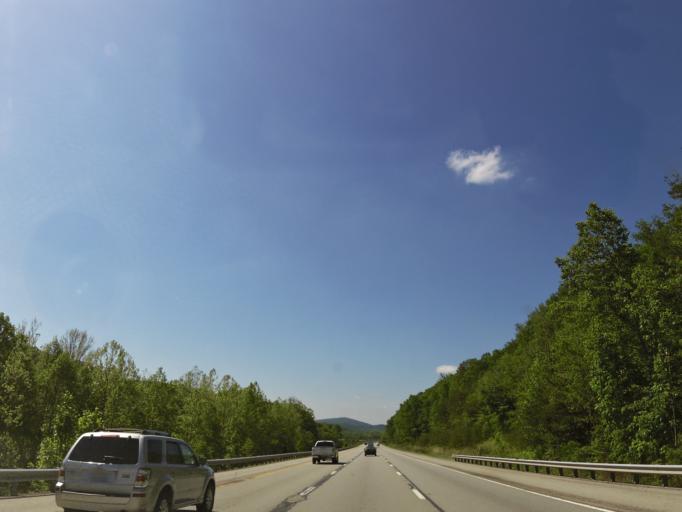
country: US
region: Kentucky
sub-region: Madison County
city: Berea
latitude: 37.5308
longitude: -84.3209
